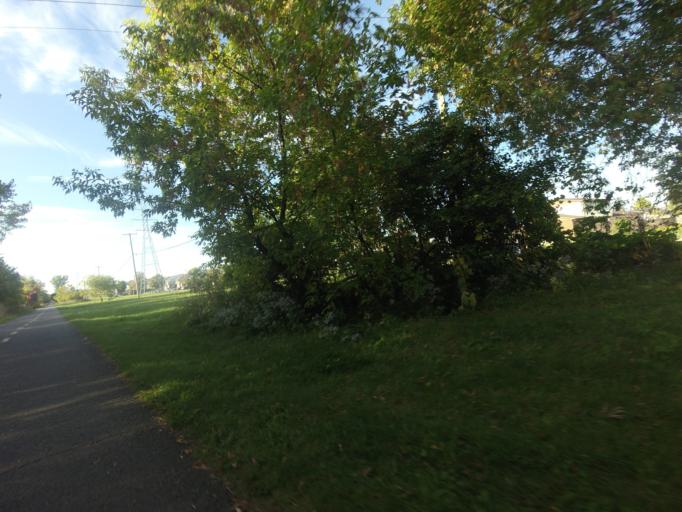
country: CA
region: Quebec
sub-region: Laurentides
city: Saint-Jerome
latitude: 45.7965
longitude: -74.0019
